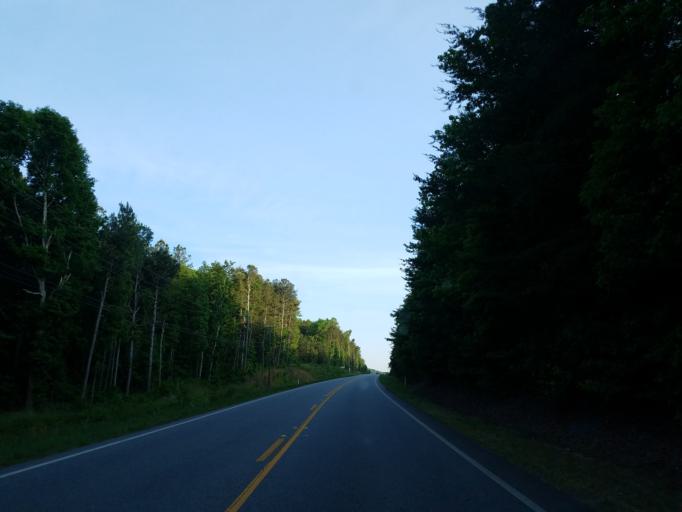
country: US
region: Georgia
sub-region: Whitfield County
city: Dalton
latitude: 34.6664
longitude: -85.0604
